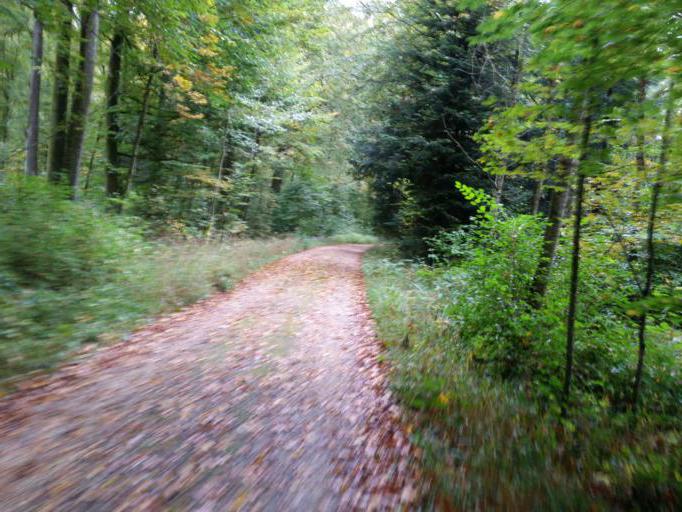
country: CH
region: Thurgau
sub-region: Arbon District
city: Uttwil
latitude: 47.5661
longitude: 9.3386
